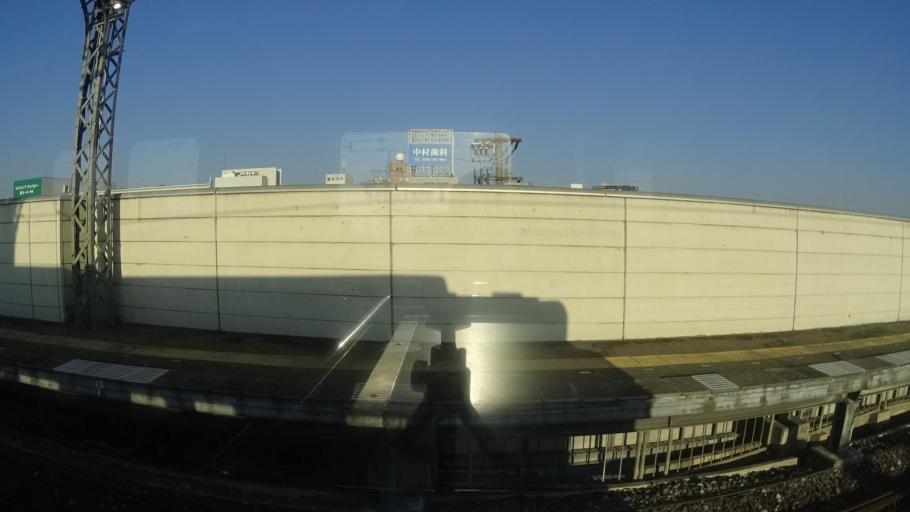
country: JP
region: Mie
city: Ise
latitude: 34.4892
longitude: 136.7138
